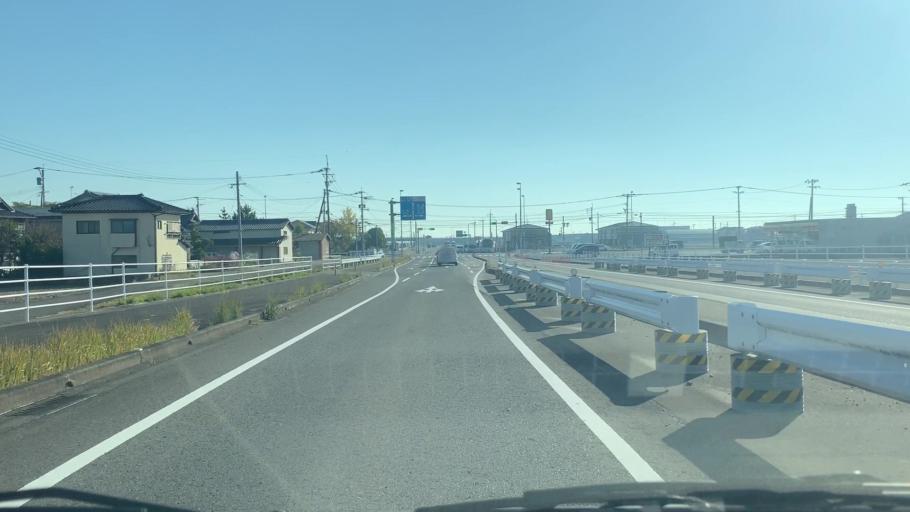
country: JP
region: Saga Prefecture
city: Saga-shi
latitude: 33.2213
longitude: 130.2071
